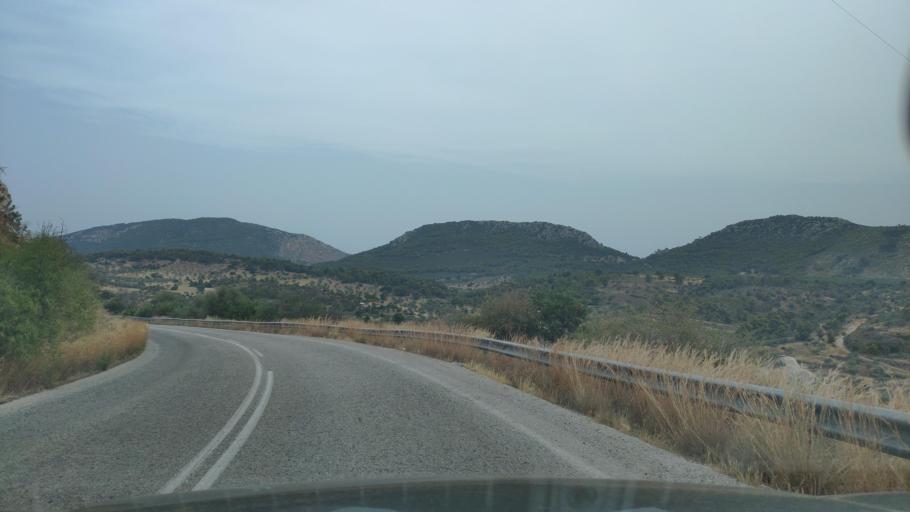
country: GR
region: Peloponnese
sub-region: Nomos Argolidos
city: Didyma
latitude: 37.4365
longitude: 23.1863
